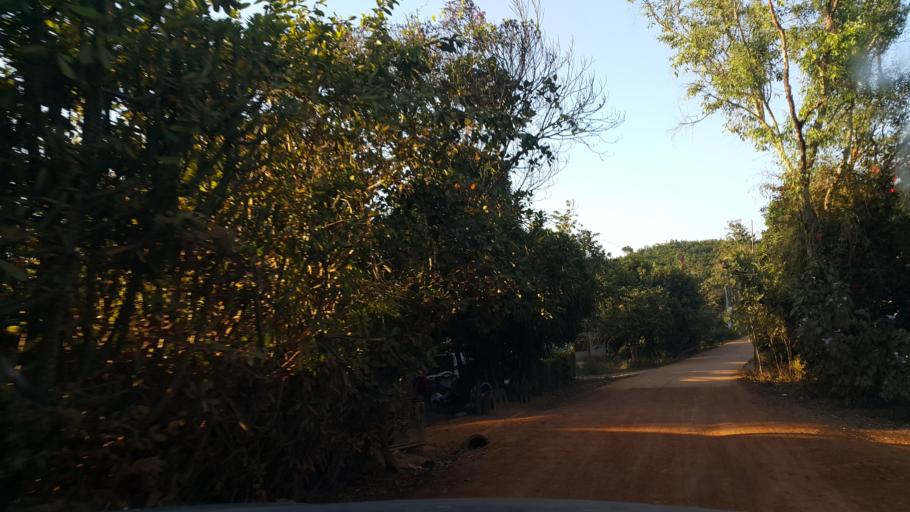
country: TH
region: Sukhothai
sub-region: Amphoe Si Satchanalai
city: Si Satchanalai
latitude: 17.6184
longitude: 99.6226
